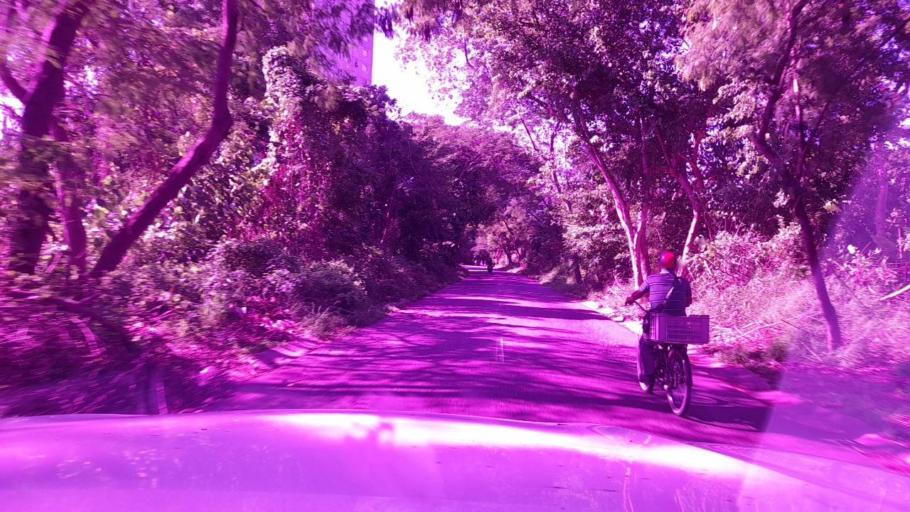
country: CU
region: La Habana
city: Alamar
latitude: 23.1634
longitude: -82.2758
